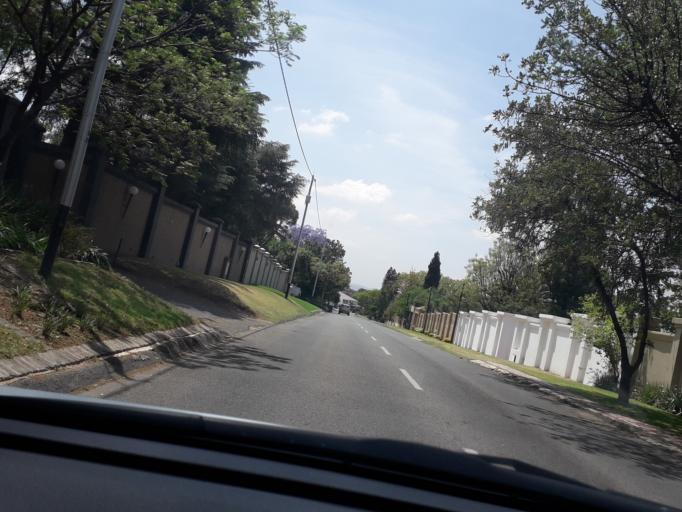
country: ZA
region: Gauteng
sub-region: City of Johannesburg Metropolitan Municipality
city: Midrand
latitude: -26.0695
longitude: 28.0219
